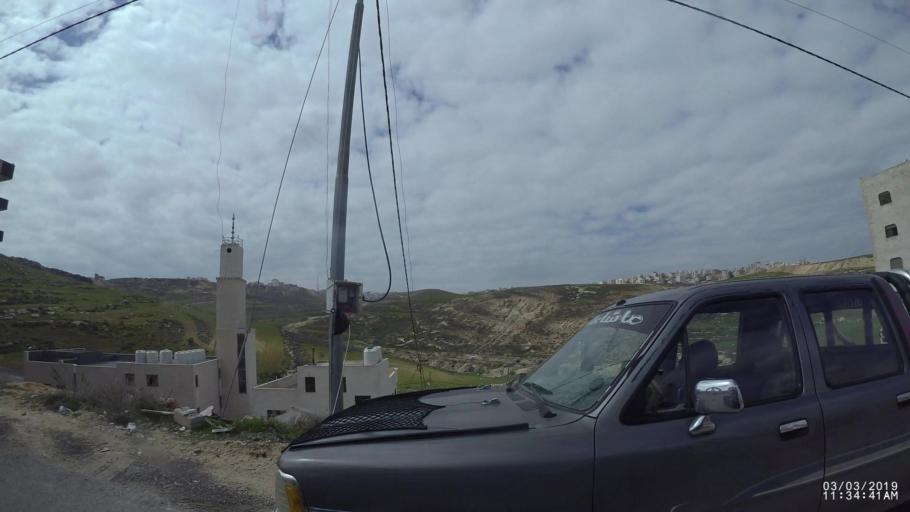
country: JO
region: Amman
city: Al Jubayhah
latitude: 32.0051
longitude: 35.9115
